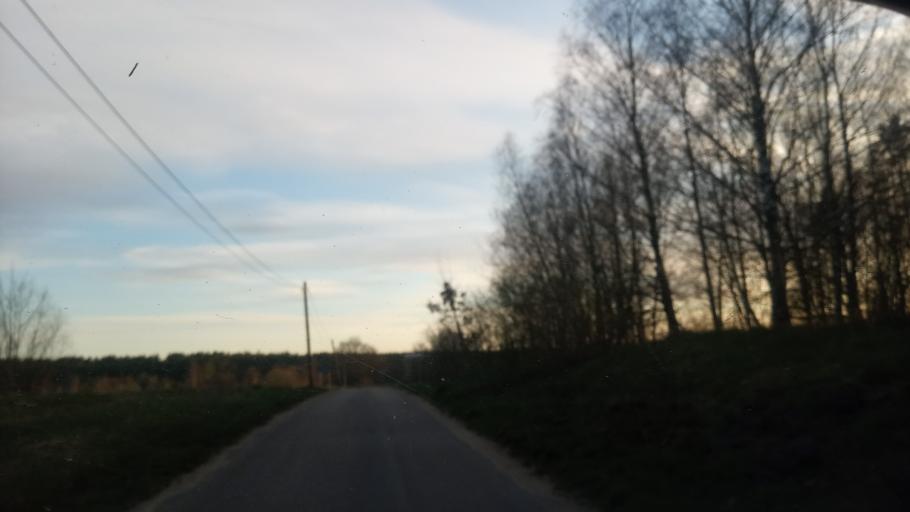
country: PL
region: West Pomeranian Voivodeship
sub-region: Powiat szczecinecki
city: Lubowo
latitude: 53.5615
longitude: 16.3901
